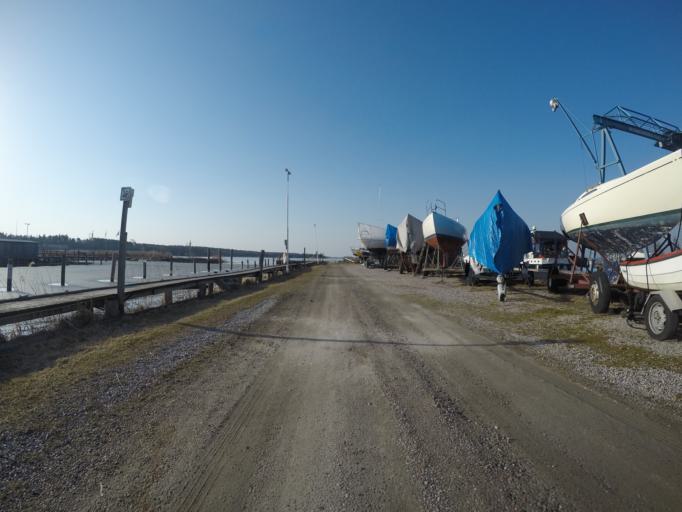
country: SE
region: Vaestmanland
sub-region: Kungsors Kommun
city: Kungsoer
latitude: 59.4299
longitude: 16.1054
